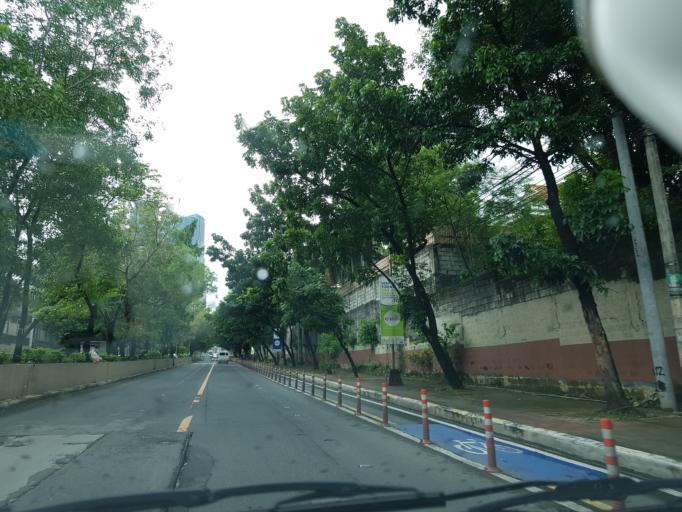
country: PH
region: Metro Manila
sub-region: Pasig
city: Pasig City
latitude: 14.5844
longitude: 121.0697
